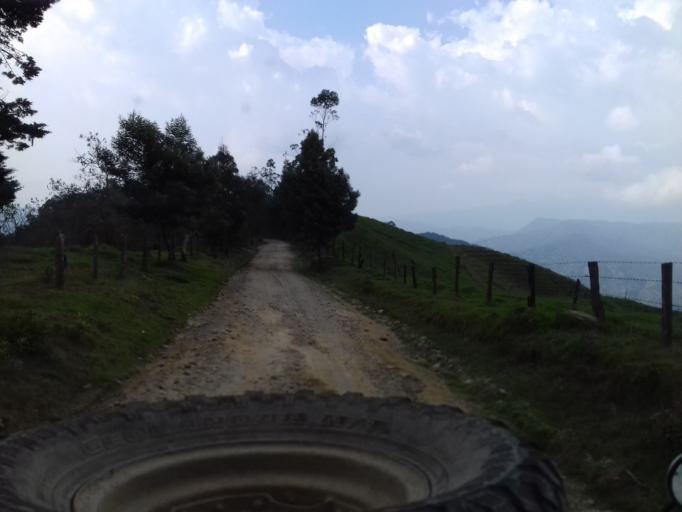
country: CO
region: Quindio
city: Salento
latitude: 4.6059
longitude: -75.5428
